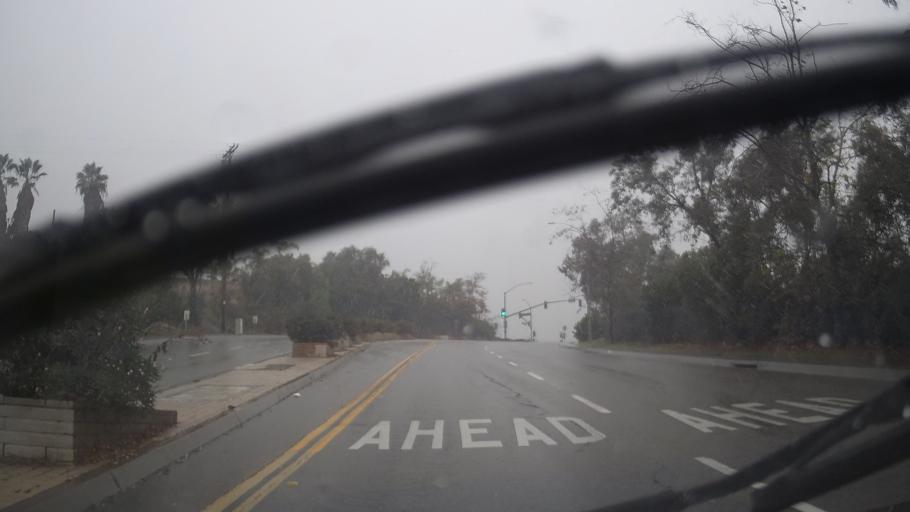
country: US
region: California
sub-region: San Diego County
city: Bonita
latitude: 32.6622
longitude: -117.0565
